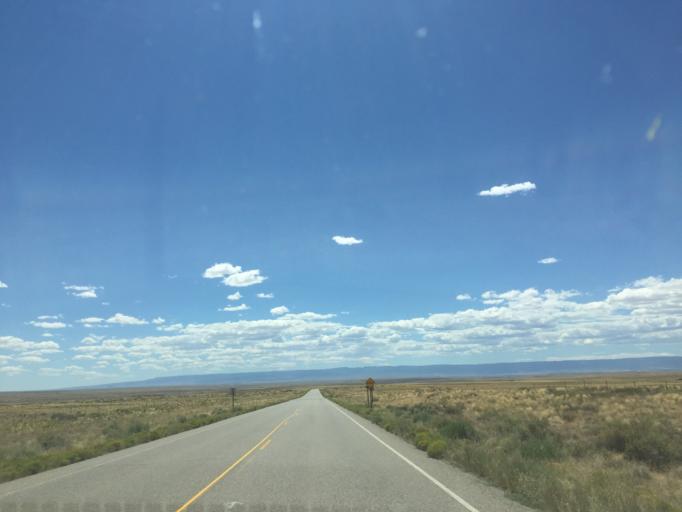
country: US
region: New Mexico
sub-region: San Juan County
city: Upper Fruitland
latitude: 36.4136
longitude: -108.4441
